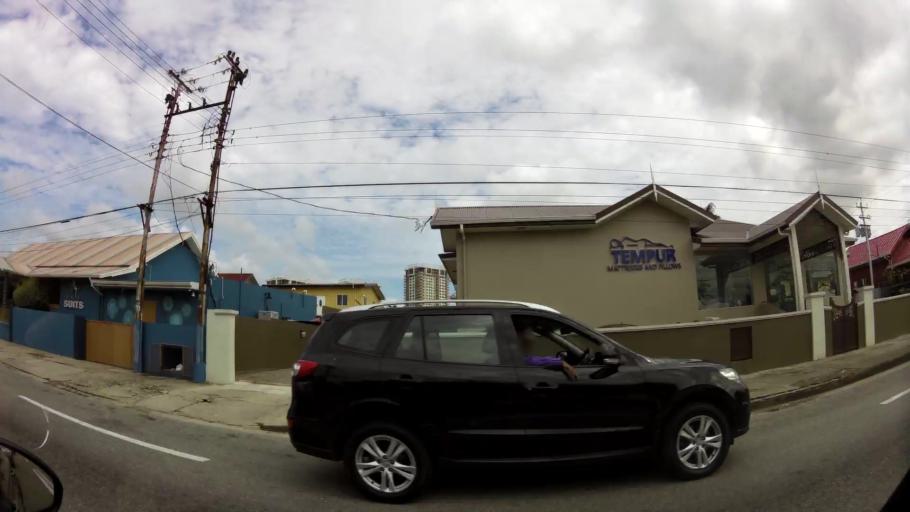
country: TT
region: City of Port of Spain
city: Mucurapo
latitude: 10.6639
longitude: -61.5287
